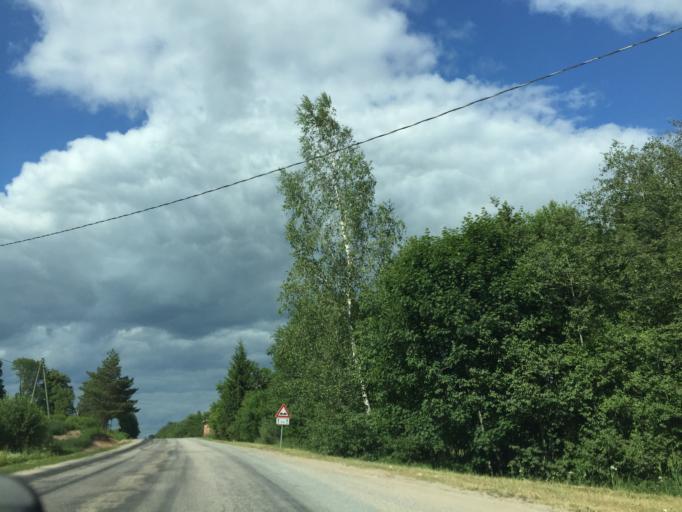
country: LV
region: Skriveri
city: Skriveri
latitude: 56.8098
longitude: 25.1132
